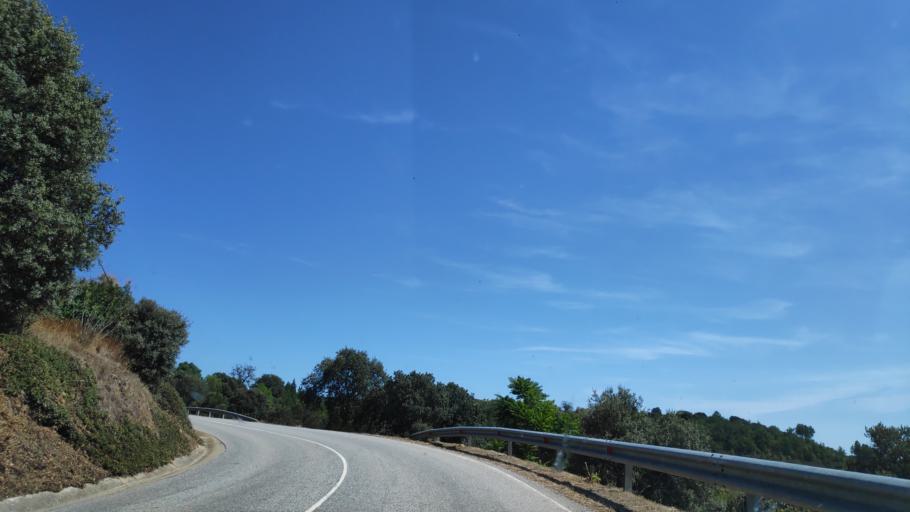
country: PT
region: Braganca
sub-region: Braganca Municipality
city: Braganca
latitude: 41.8367
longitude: -6.7470
